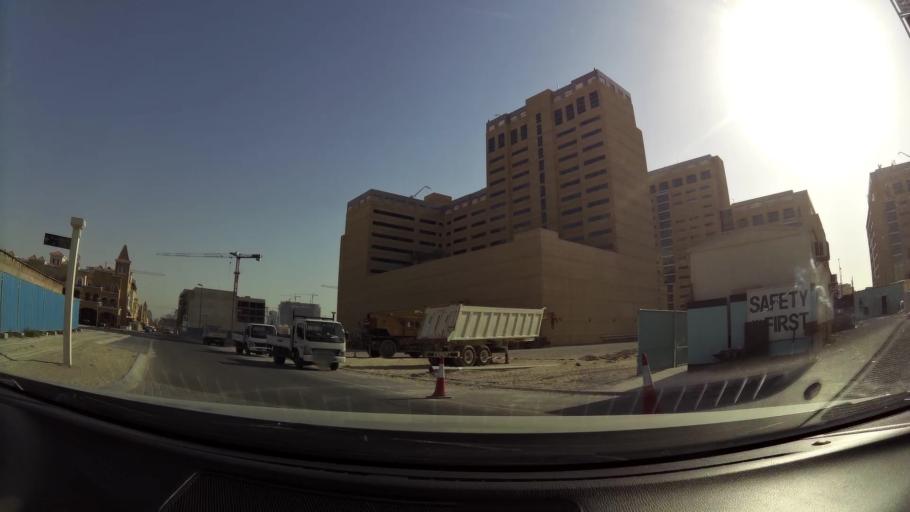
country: AE
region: Dubai
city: Dubai
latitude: 25.0668
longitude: 55.2115
